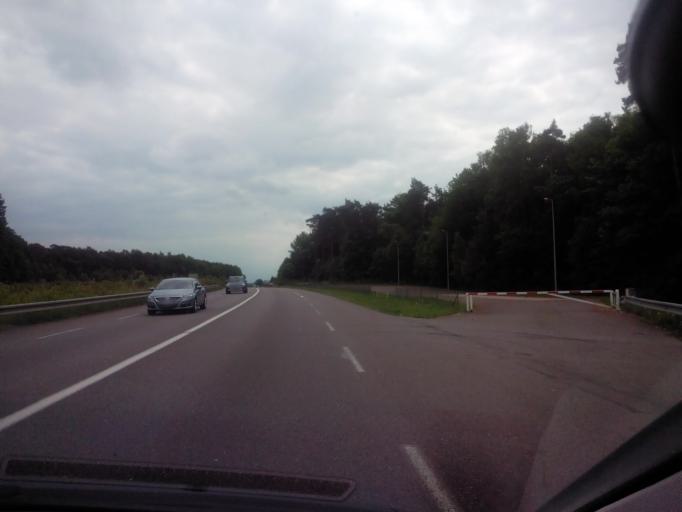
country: FR
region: Lorraine
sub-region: Departement de la Moselle
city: Carling
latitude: 49.1849
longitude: 6.7107
